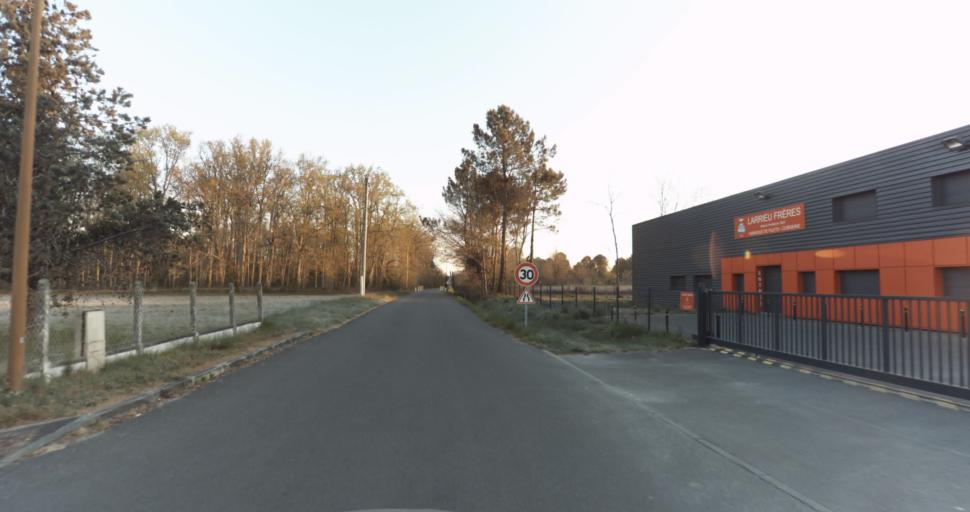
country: FR
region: Aquitaine
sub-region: Departement de la Gironde
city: Martignas-sur-Jalle
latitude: 44.8164
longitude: -0.7442
